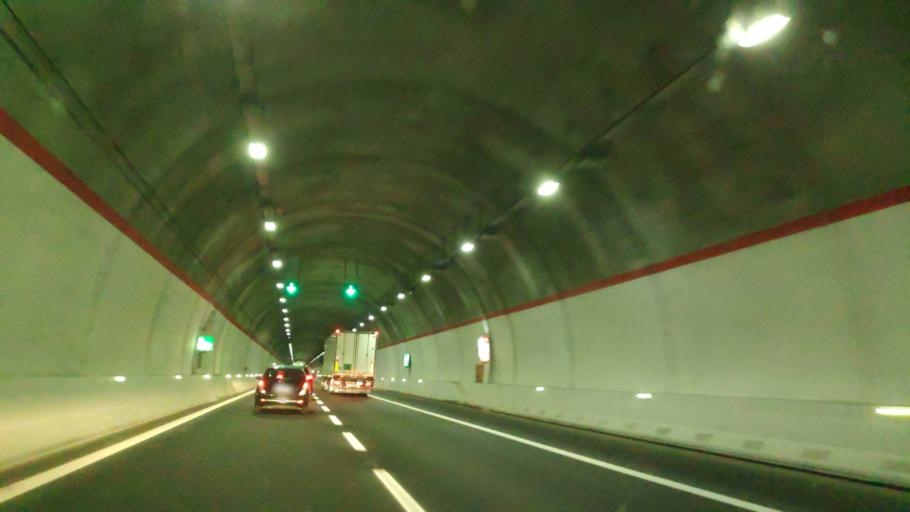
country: IT
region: Basilicate
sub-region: Provincia di Potenza
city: Lagonegro
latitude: 40.1416
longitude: 15.7567
